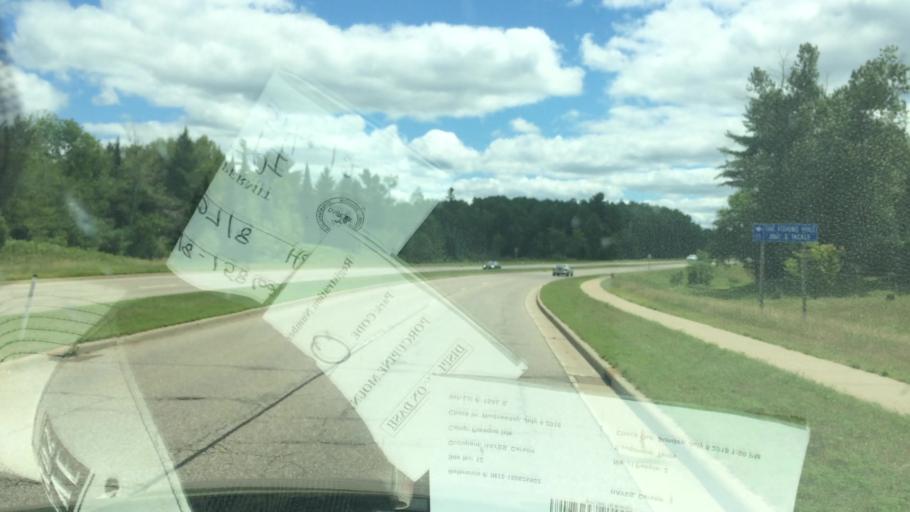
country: US
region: Wisconsin
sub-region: Oneida County
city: Rhinelander
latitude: 45.6418
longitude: -89.3806
